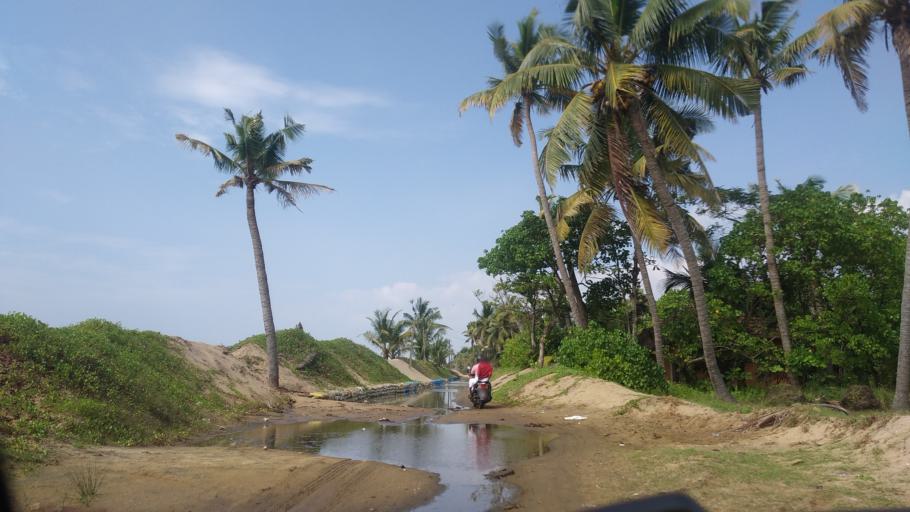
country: IN
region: Kerala
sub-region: Ernakulam
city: Elur
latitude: 10.0722
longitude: 76.1971
